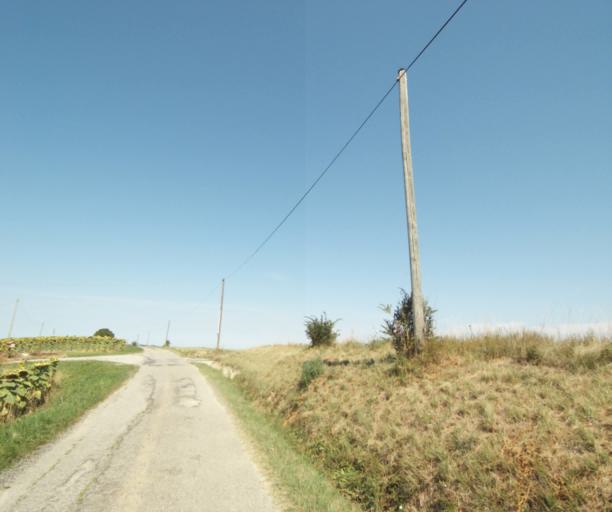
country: FR
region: Midi-Pyrenees
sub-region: Departement de l'Ariege
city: Lezat-sur-Leze
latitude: 43.2452
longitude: 1.3916
